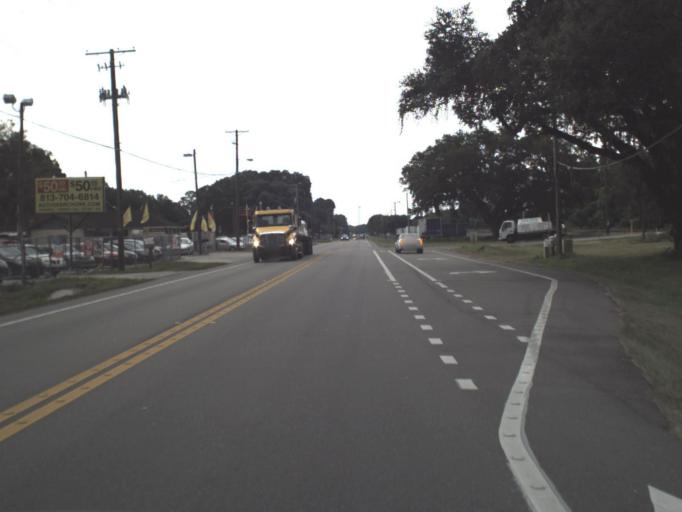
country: US
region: Florida
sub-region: Hillsborough County
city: Plant City
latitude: 28.0249
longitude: -82.0692
